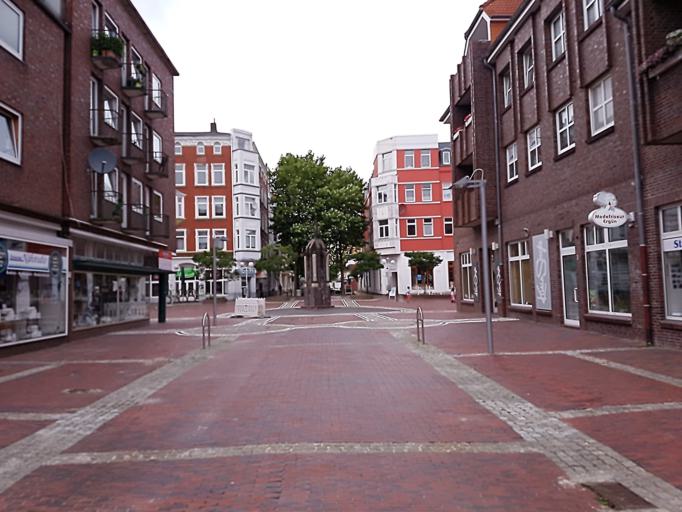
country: DE
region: Lower Saxony
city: Wilhelmshaven
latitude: 53.5203
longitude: 8.1124
